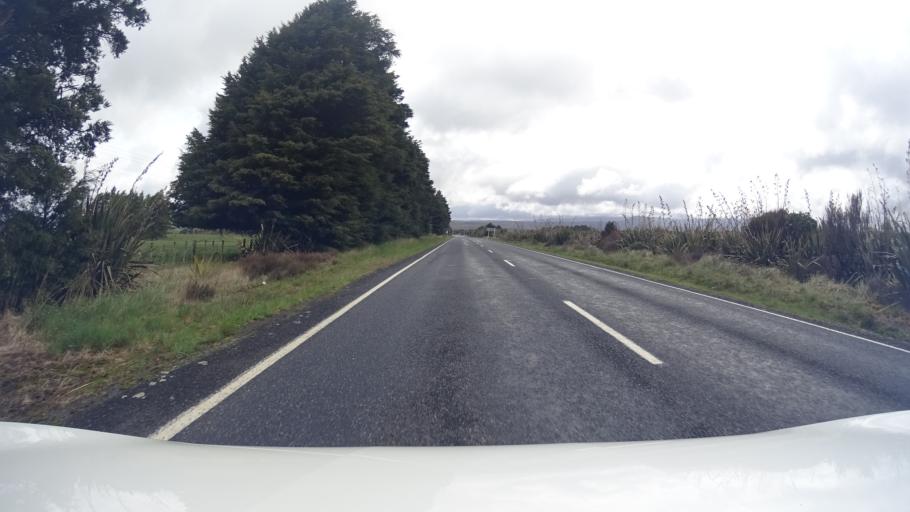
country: NZ
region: Manawatu-Wanganui
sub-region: Ruapehu District
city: Waiouru
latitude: -39.1639
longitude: 175.4882
